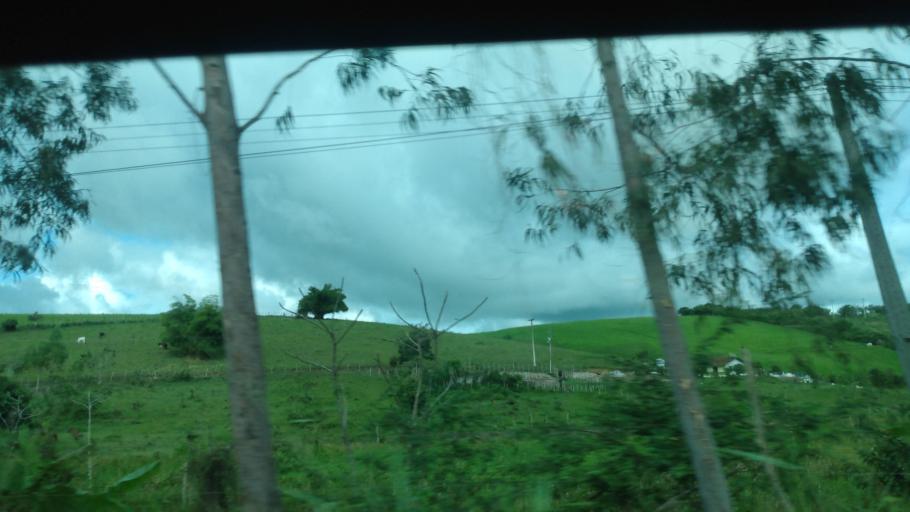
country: BR
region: Pernambuco
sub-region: Quipapa
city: Quipapa
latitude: -8.7783
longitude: -35.9330
